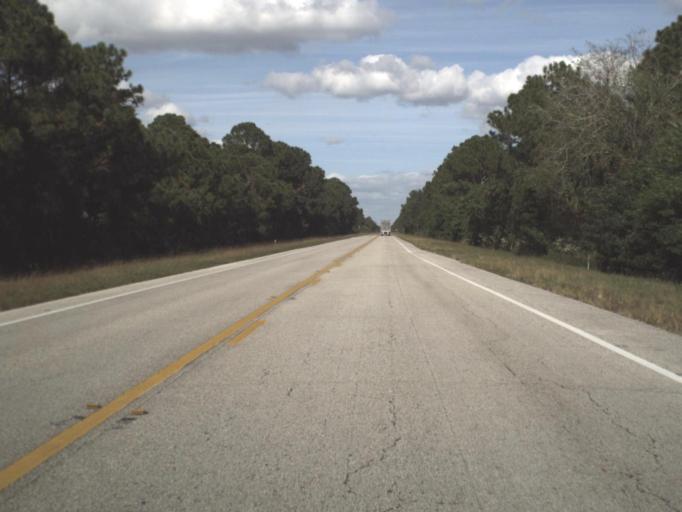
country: US
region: Florida
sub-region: Brevard County
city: Port Saint John
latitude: 28.5075
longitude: -80.8347
